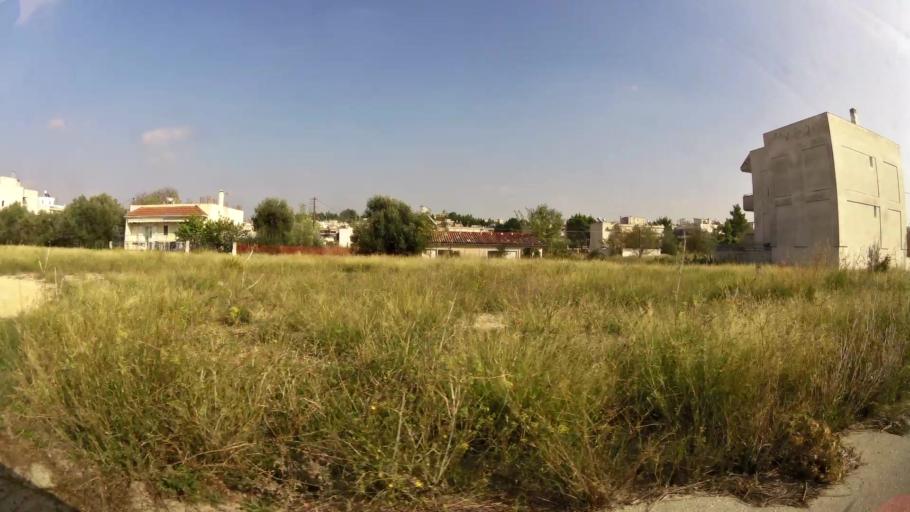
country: GR
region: Attica
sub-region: Nomarchia Dytikis Attikis
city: Zefyri
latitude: 38.0826
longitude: 23.7164
